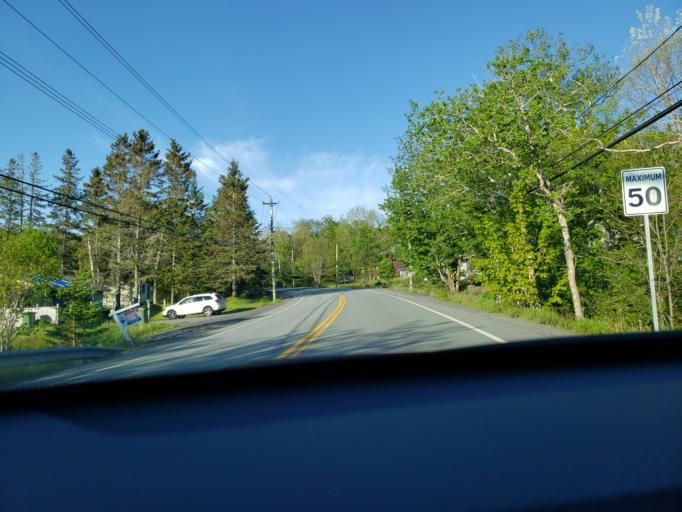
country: CA
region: Nova Scotia
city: Cole Harbour
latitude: 44.7335
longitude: -63.3922
